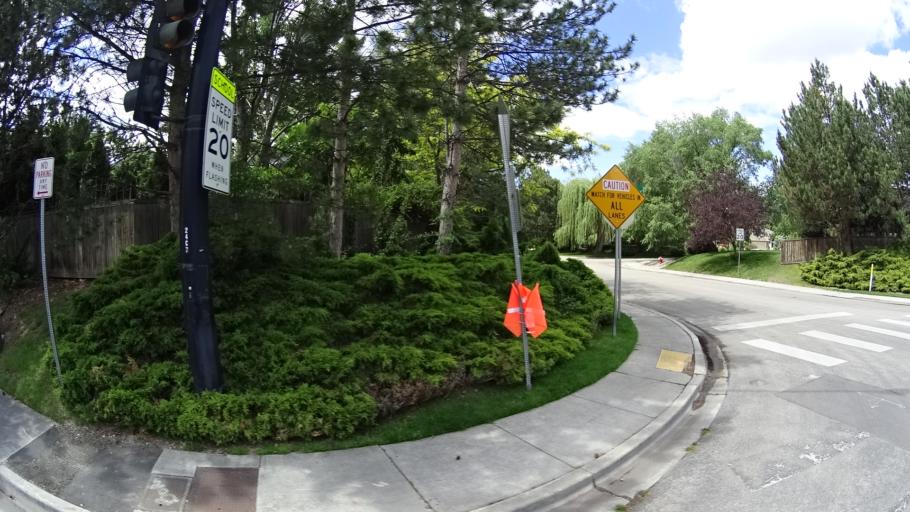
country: US
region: Idaho
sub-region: Ada County
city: Boise
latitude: 43.5772
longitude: -116.1579
